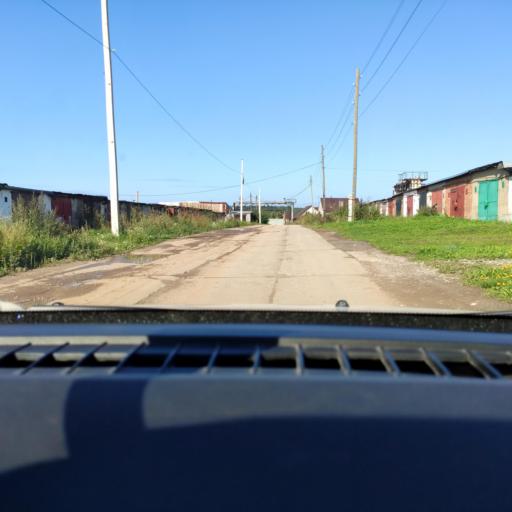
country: RU
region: Perm
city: Novyye Lyady
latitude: 58.0551
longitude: 56.5844
